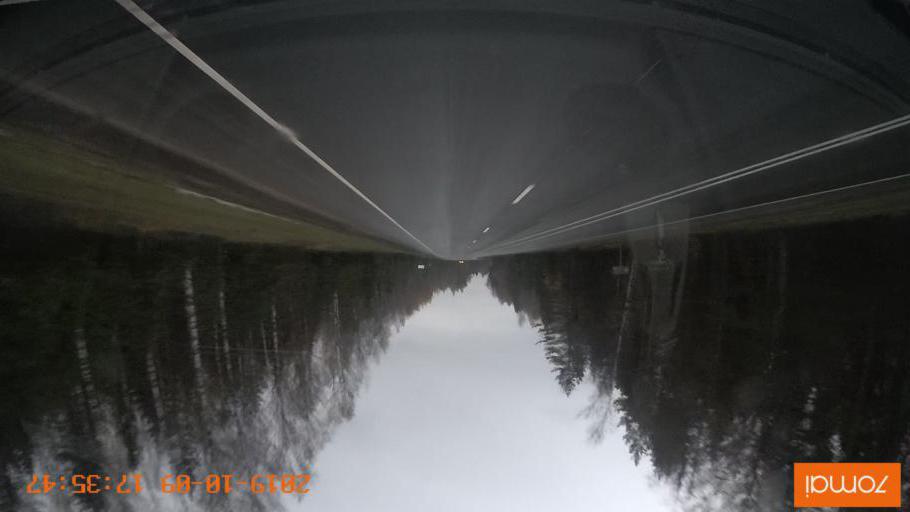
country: RU
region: Ivanovo
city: Bogorodskoye
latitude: 57.0881
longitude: 40.9997
